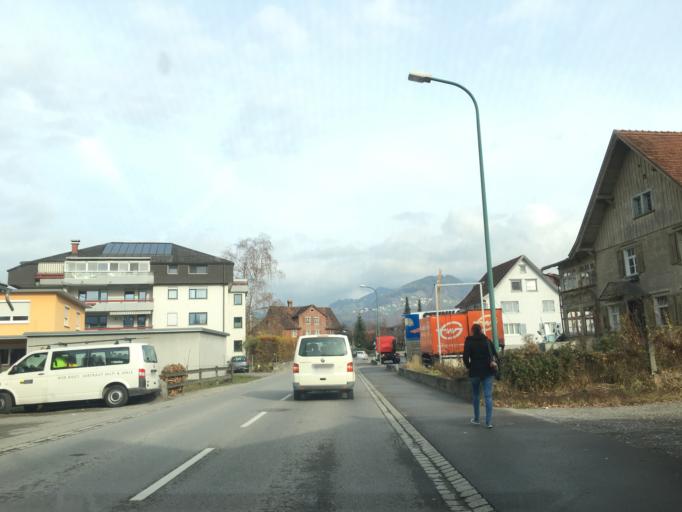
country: AT
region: Vorarlberg
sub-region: Politischer Bezirk Feldkirch
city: Rankweil
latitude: 47.2733
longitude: 9.6488
